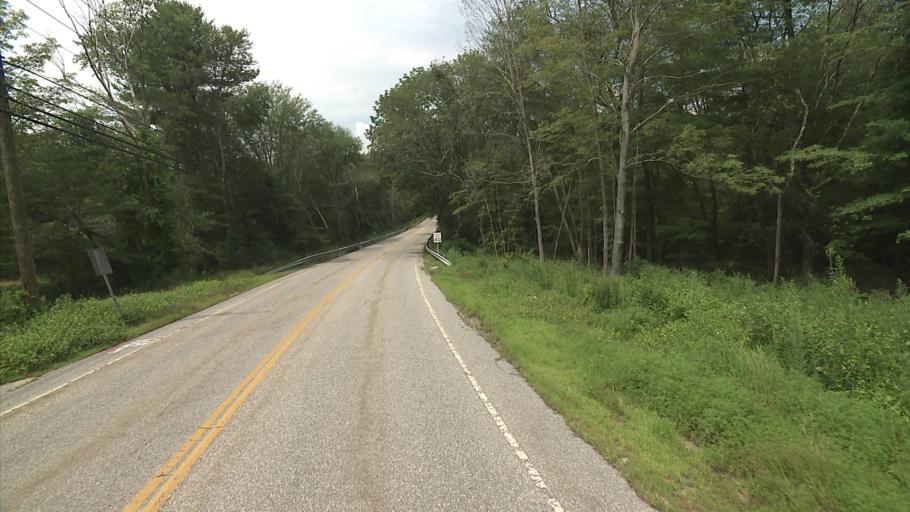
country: US
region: Connecticut
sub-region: Windham County
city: Danielson
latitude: 41.8027
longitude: -71.8565
